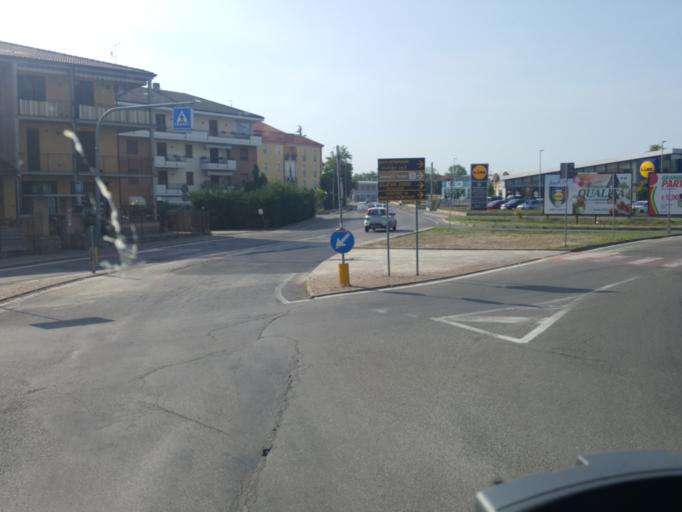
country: IT
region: Piedmont
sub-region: Provincia di Alessandria
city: Tortona
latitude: 44.8855
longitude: 8.8569
